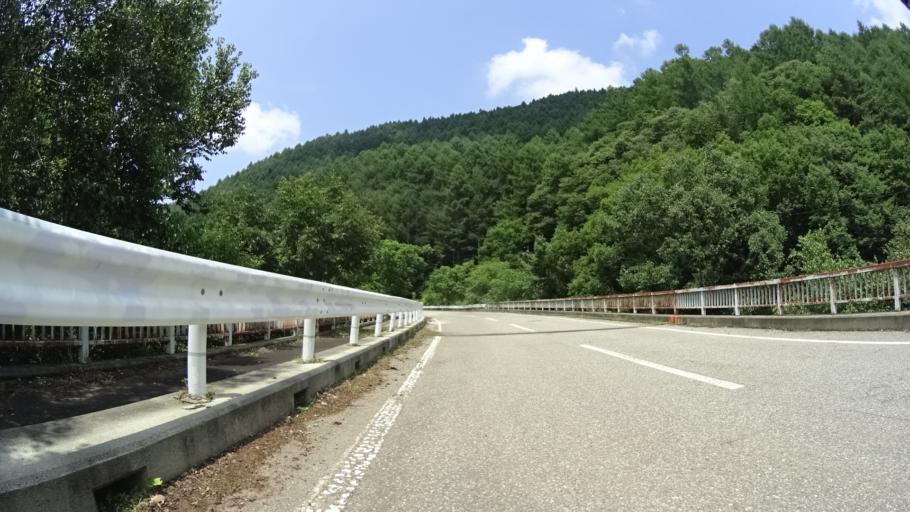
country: JP
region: Nagano
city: Saku
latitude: 36.1234
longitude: 138.6057
